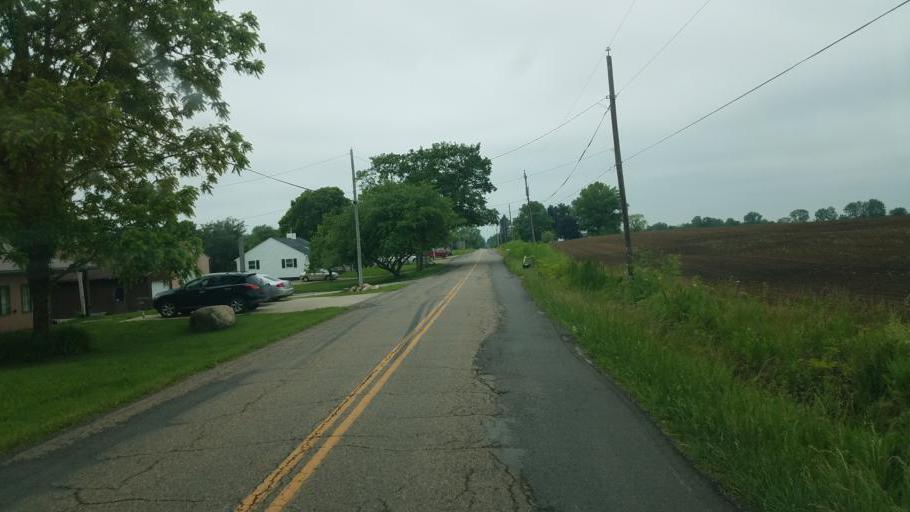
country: US
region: Ohio
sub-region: Knox County
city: Centerburg
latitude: 40.3218
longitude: -82.7292
